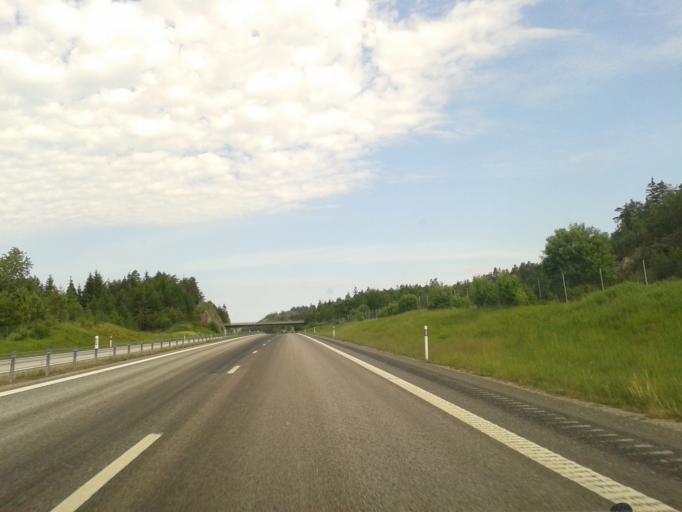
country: SE
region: Vaestra Goetaland
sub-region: Lysekils Kommun
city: Brastad
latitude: 58.5469
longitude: 11.5139
